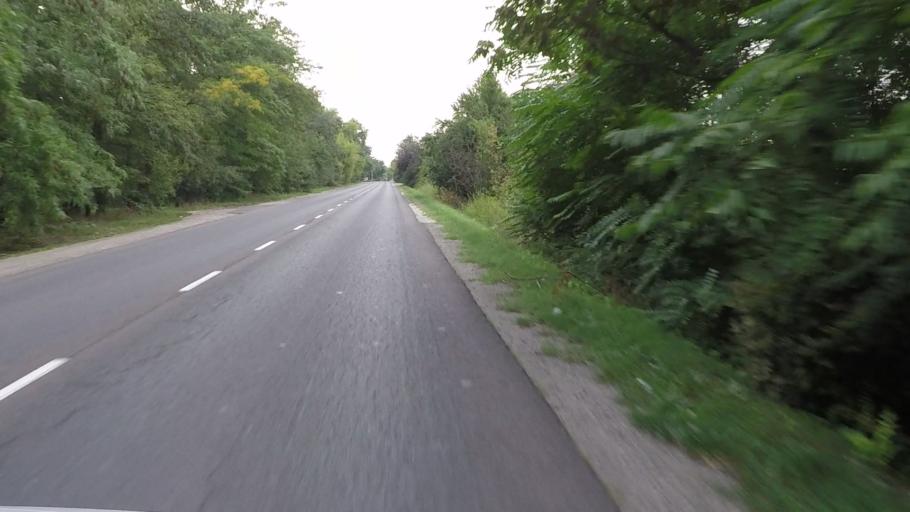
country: HU
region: Jasz-Nagykun-Szolnok
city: Szolnok
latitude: 47.1948
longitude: 20.1693
